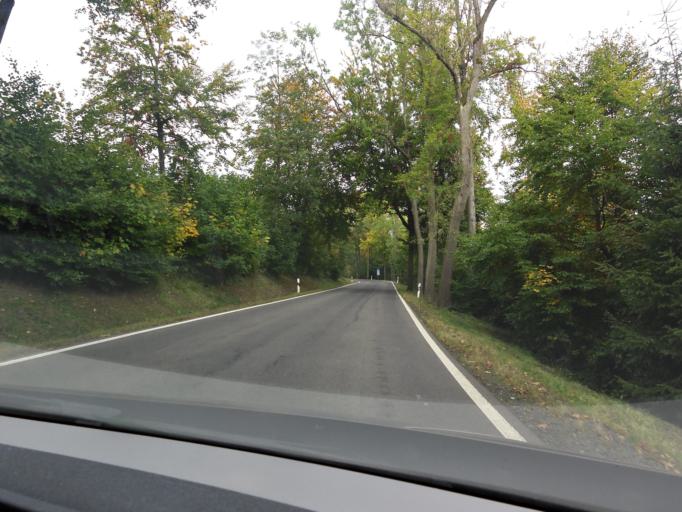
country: DE
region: Thuringia
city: Brotterode
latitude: 50.8180
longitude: 10.4633
